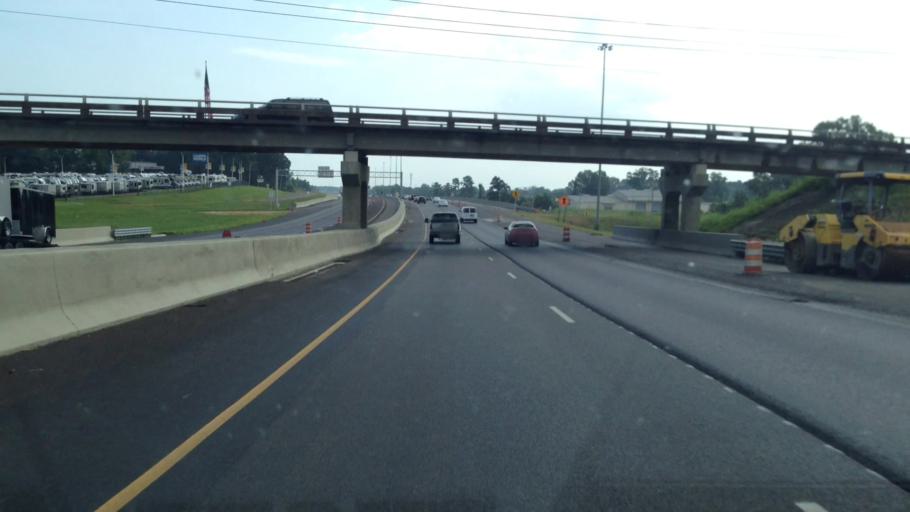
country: US
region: Mississippi
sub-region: Hinds County
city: Byram
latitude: 32.2209
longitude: -90.2263
